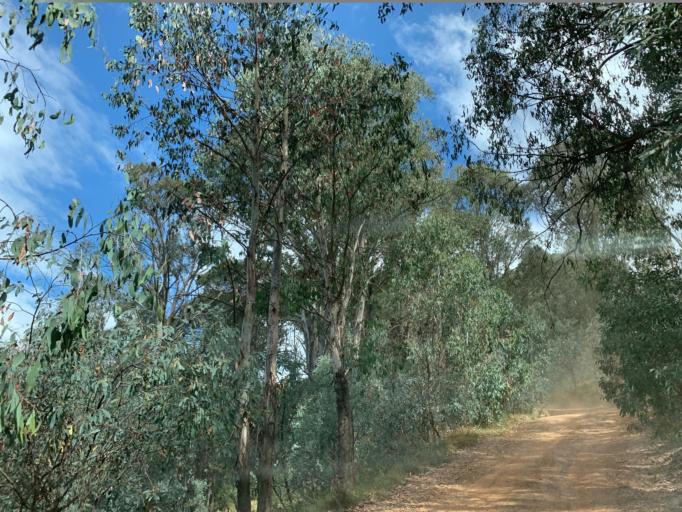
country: AU
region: Victoria
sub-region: Mansfield
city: Mansfield
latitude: -37.1075
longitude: 146.5356
